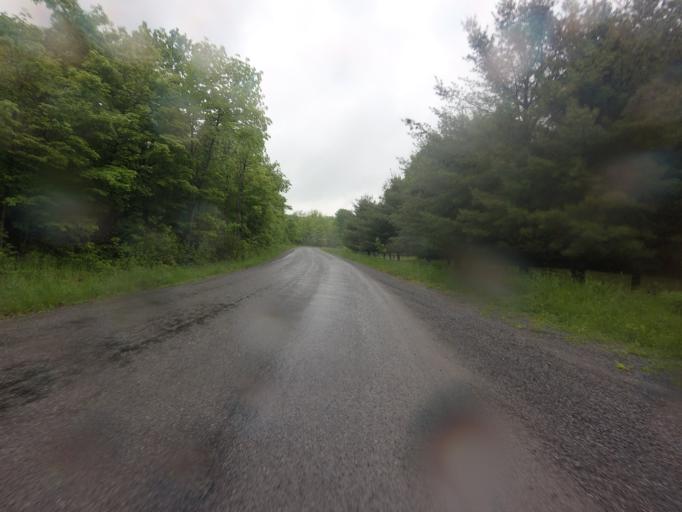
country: CA
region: Ontario
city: Gananoque
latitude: 44.5403
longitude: -76.3696
